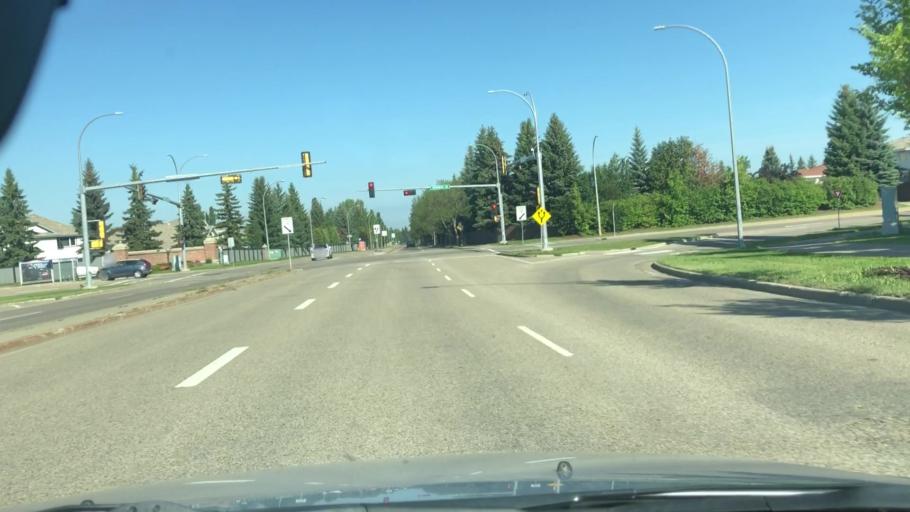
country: CA
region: Alberta
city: Edmonton
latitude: 53.4717
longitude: -113.5933
